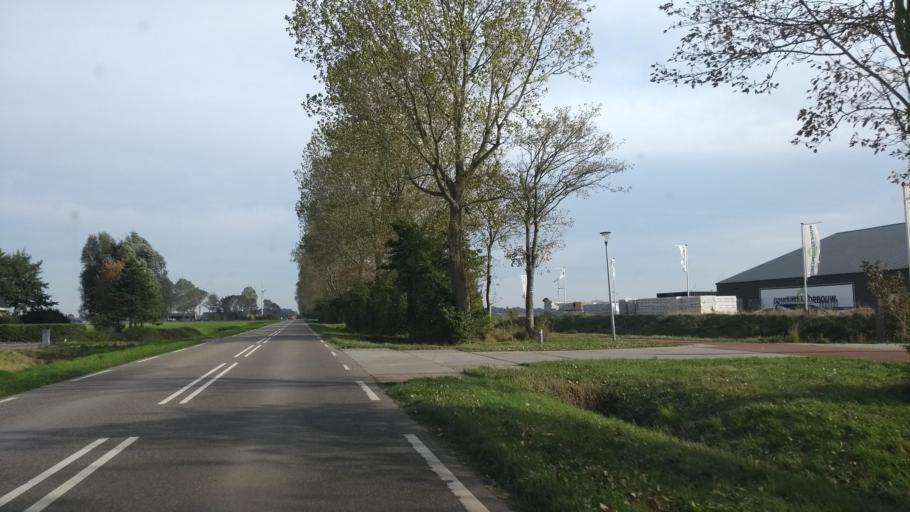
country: NL
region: North Holland
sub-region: Gemeente Schagen
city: Harenkarspel
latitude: 52.7197
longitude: 4.7523
